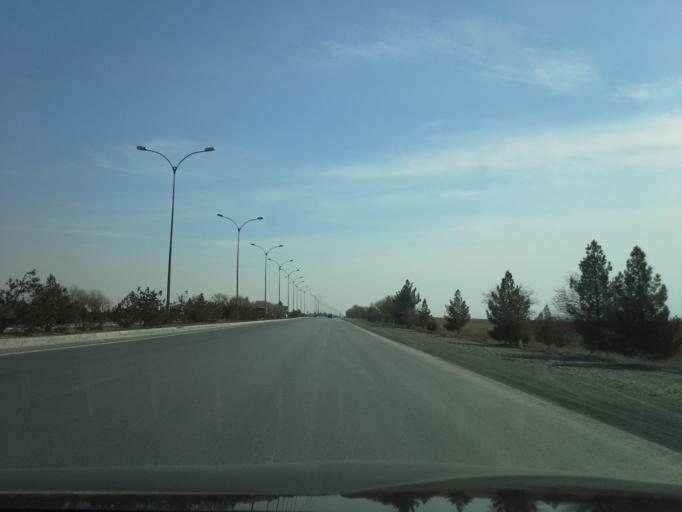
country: TM
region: Ahal
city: Abadan
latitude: 38.1262
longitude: 58.0317
